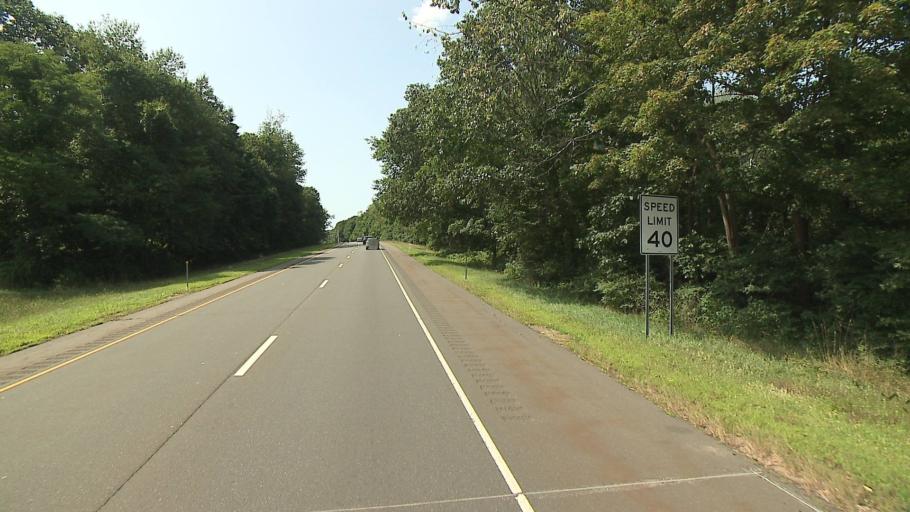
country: US
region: Connecticut
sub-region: Fairfield County
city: Trumbull
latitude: 41.2864
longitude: -73.2296
